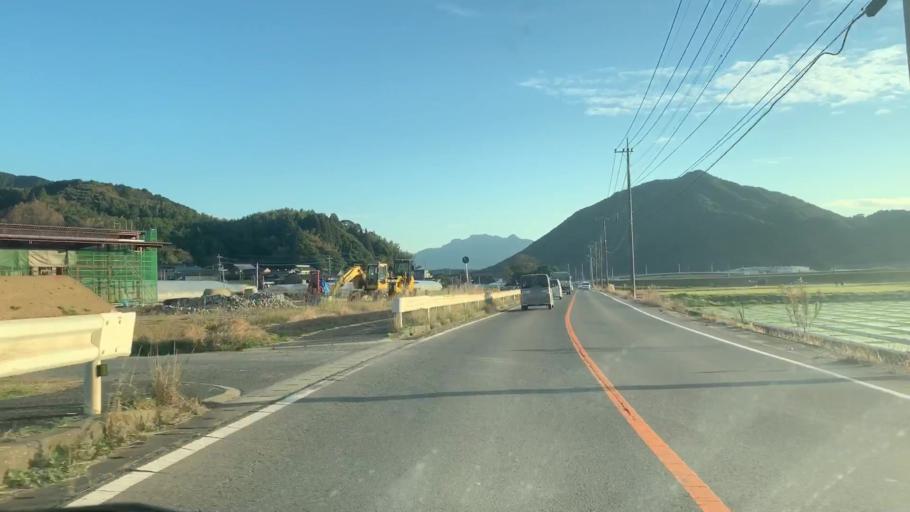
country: JP
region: Saga Prefecture
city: Karatsu
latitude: 33.3797
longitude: 129.9993
